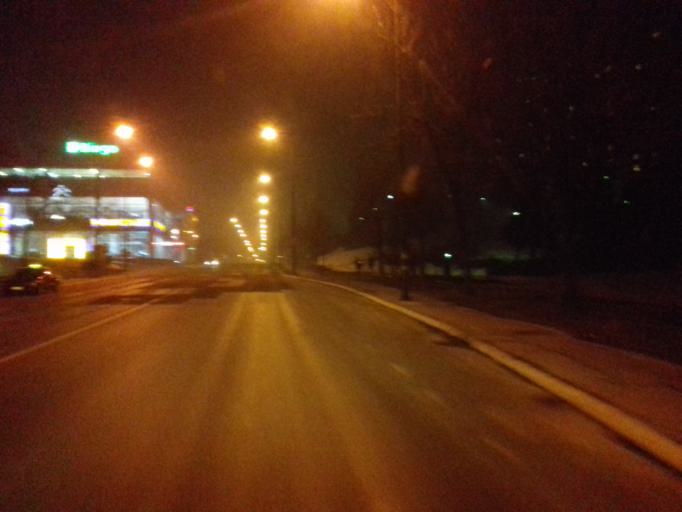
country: BA
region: Federation of Bosnia and Herzegovina
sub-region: Kanton Sarajevo
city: Sarajevo
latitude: 43.8448
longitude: 18.3477
